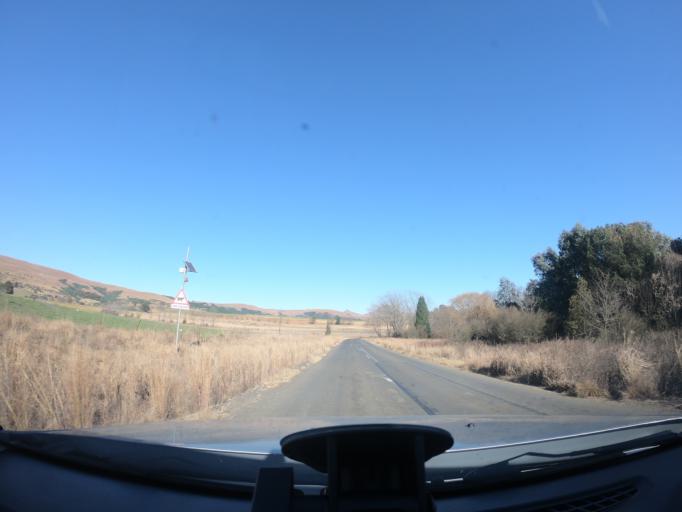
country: ZA
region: KwaZulu-Natal
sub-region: uMgungundlovu District Municipality
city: Mooirivier
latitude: -29.3279
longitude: 29.8494
